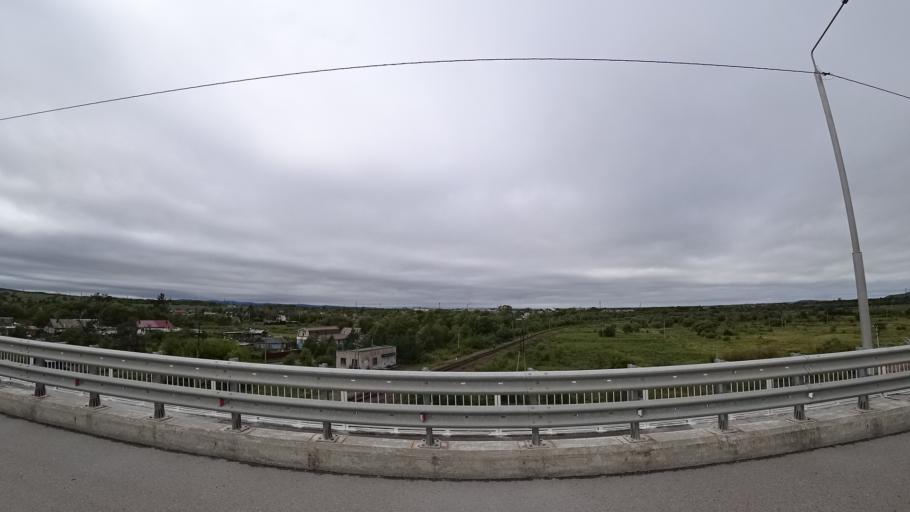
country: RU
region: Primorskiy
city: Monastyrishche
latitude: 44.1920
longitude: 132.4419
